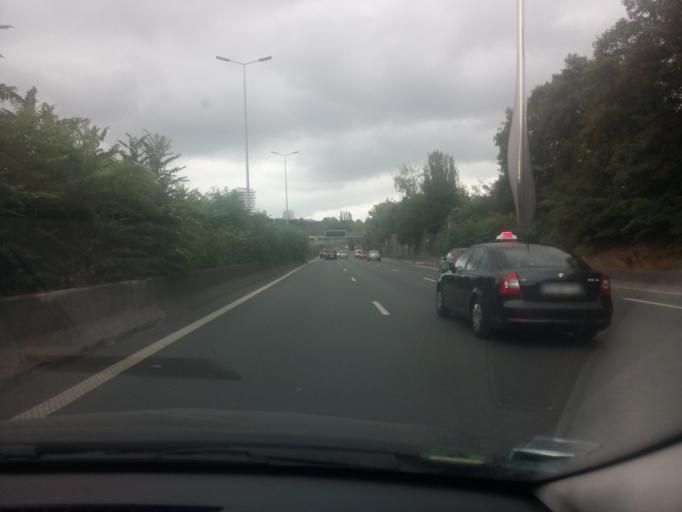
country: FR
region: Ile-de-France
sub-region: Departement du Val-de-Marne
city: Gentilly
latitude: 48.8098
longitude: 2.3385
